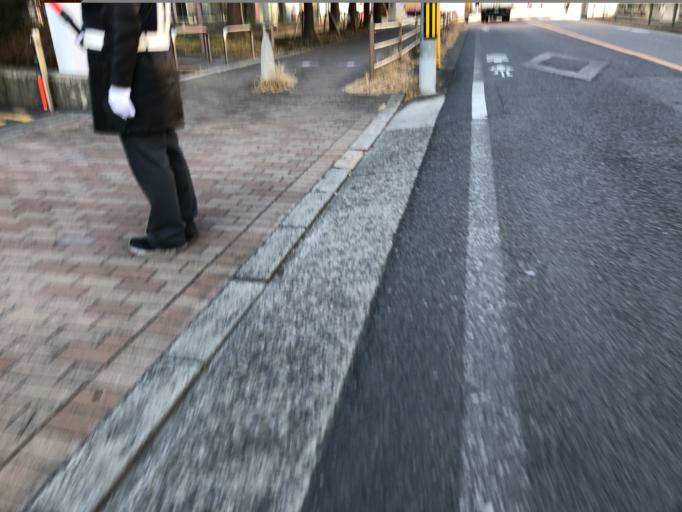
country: JP
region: Tokyo
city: Kamirenjaku
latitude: 35.7014
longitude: 139.5465
